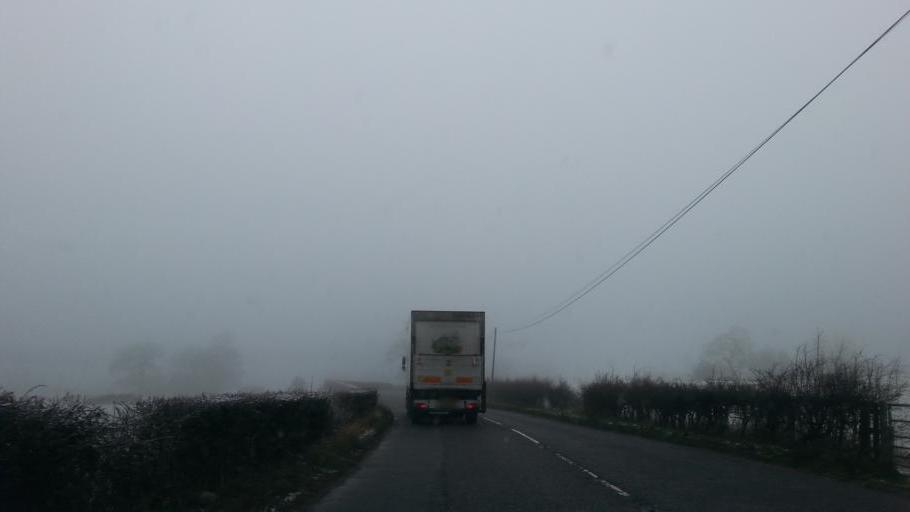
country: GB
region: England
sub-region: Cheshire East
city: Eaton
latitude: 53.1942
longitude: -2.2202
